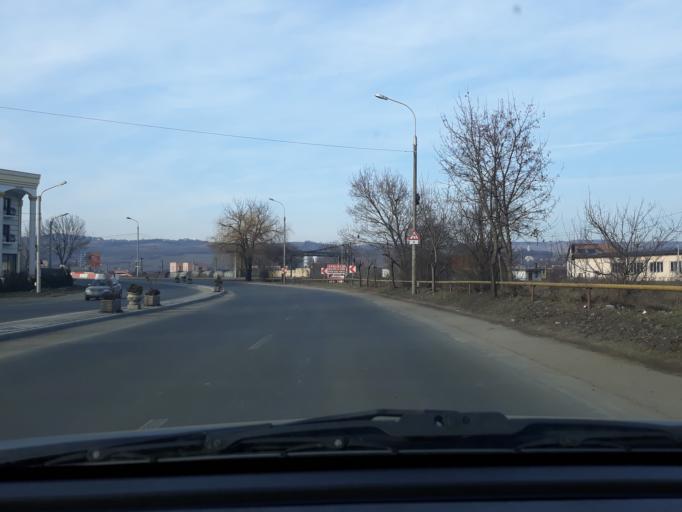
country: RO
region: Salaj
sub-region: Comuna Criseni
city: Criseni
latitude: 47.2215
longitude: 23.0402
